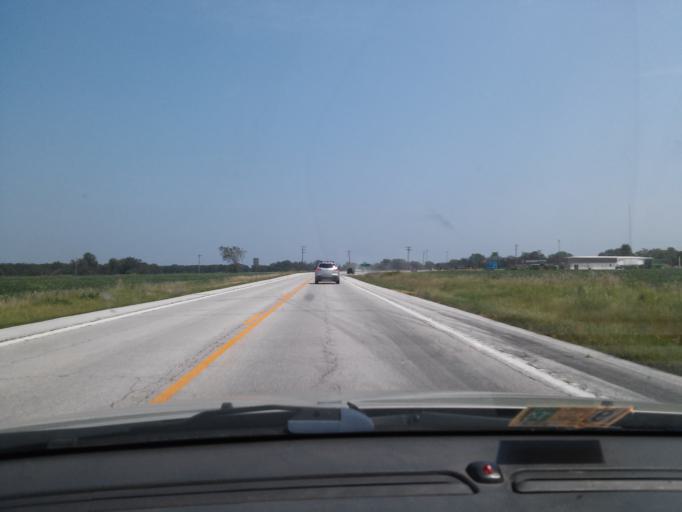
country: US
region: Missouri
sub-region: Audrain County
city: Vandalia
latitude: 39.3444
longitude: -91.4157
